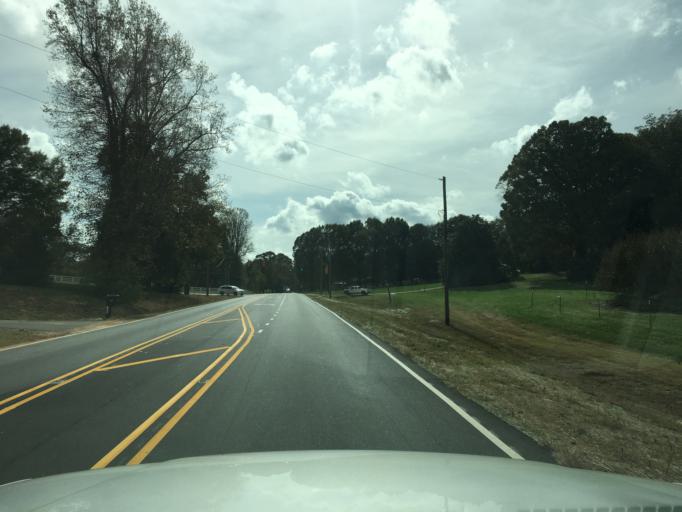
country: US
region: North Carolina
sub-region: Catawba County
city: Newton
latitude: 35.6785
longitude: -81.2732
